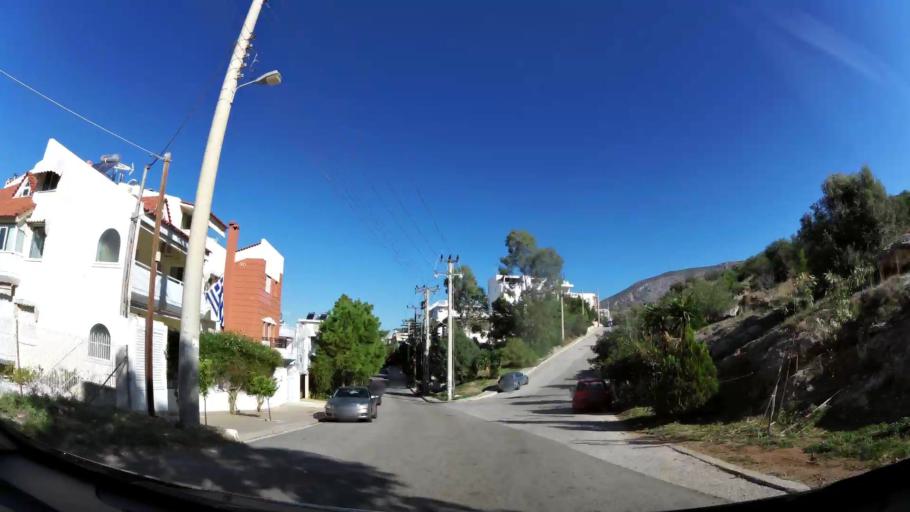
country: GR
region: Attica
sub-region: Nomarchia Athinas
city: Glyfada
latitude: 37.8596
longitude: 23.7710
